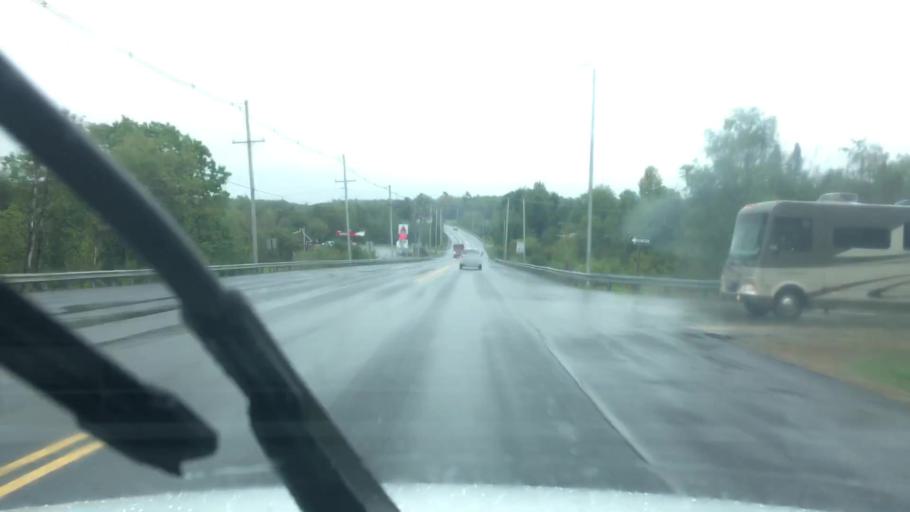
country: US
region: Maine
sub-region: Penobscot County
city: Hampden
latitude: 44.7718
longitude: -68.8579
